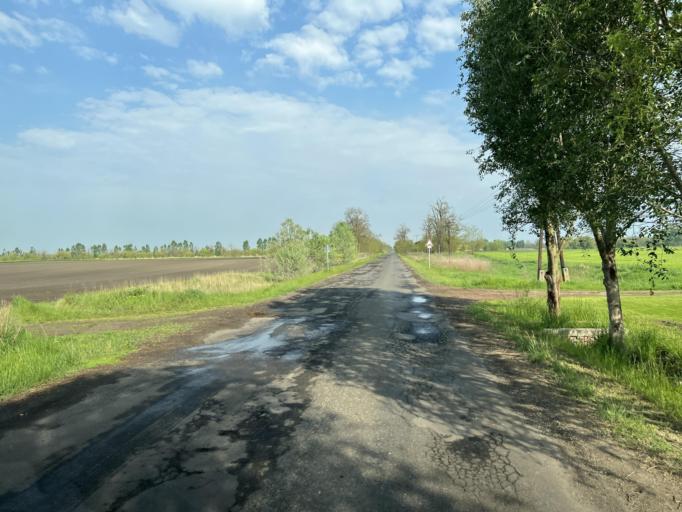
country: HU
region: Pest
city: Abony
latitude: 47.1651
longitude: 20.0385
